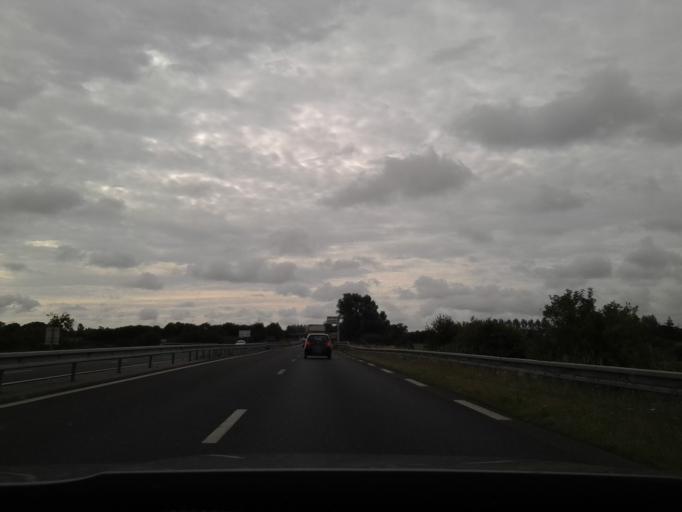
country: FR
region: Lower Normandy
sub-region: Departement de la Manche
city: Saint-Hilaire-Petitville
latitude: 49.3120
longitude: -1.2258
